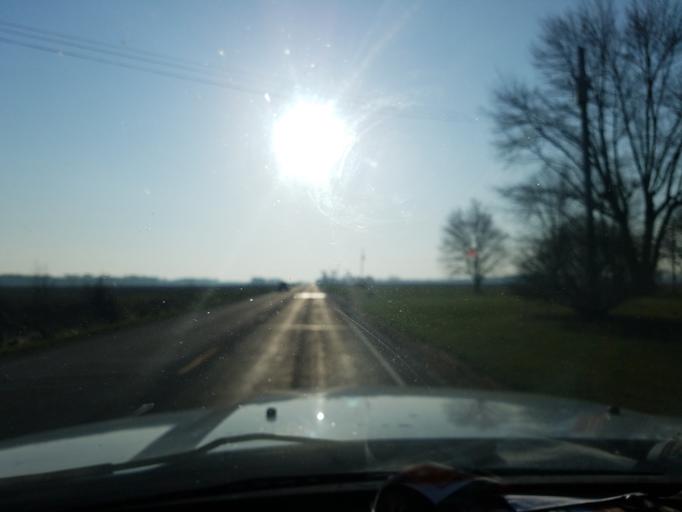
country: US
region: Indiana
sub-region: Vigo County
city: Seelyville
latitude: 39.3890
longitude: -87.1987
